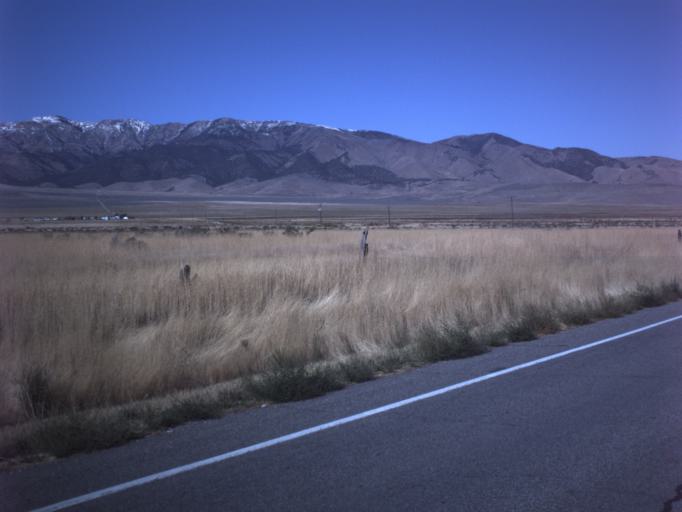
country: US
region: Utah
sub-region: Tooele County
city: Grantsville
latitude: 40.6069
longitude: -112.4892
